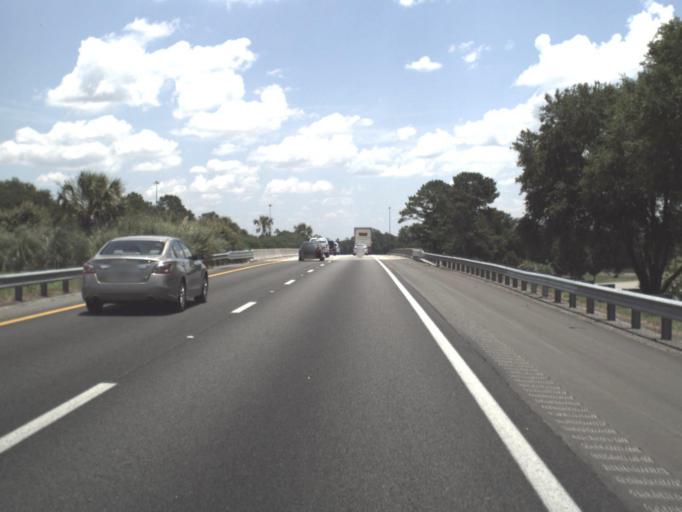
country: US
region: Florida
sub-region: Madison County
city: Madison
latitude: 30.3957
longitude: -83.3573
